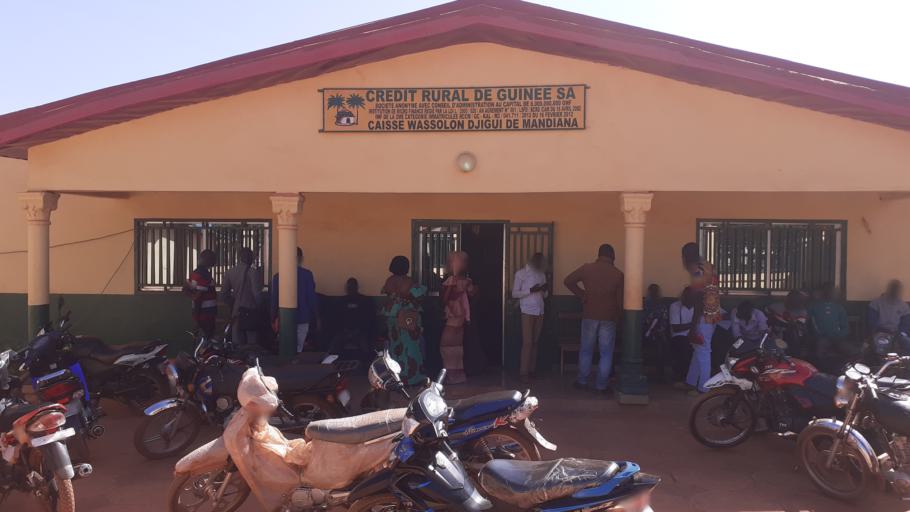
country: GN
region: Kankan
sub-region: Mandiana Prefecture
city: Mandiana
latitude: 10.6116
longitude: -8.6964
